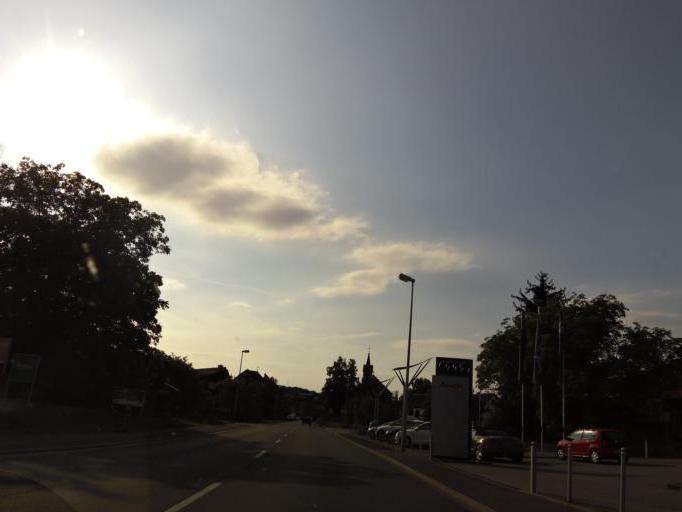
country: DE
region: Bavaria
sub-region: Regierungsbezirk Unterfranken
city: Marktheidenfeld
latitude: 49.8415
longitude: 9.6061
